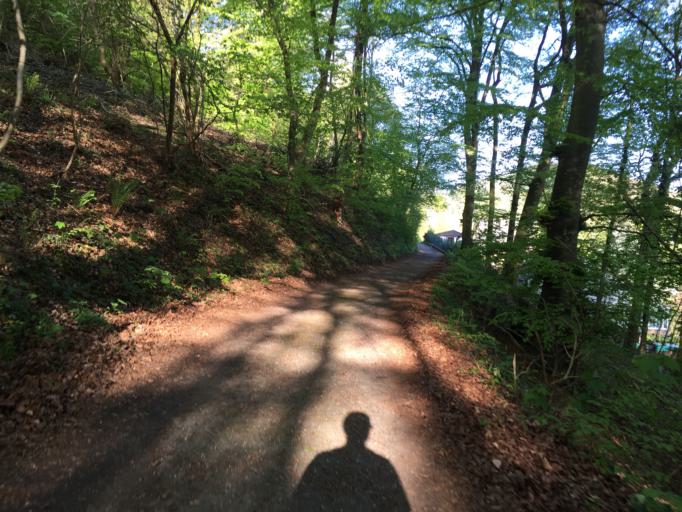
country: DE
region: Baden-Wuerttemberg
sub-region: Karlsruhe Region
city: Weinheim
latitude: 49.5230
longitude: 8.6790
